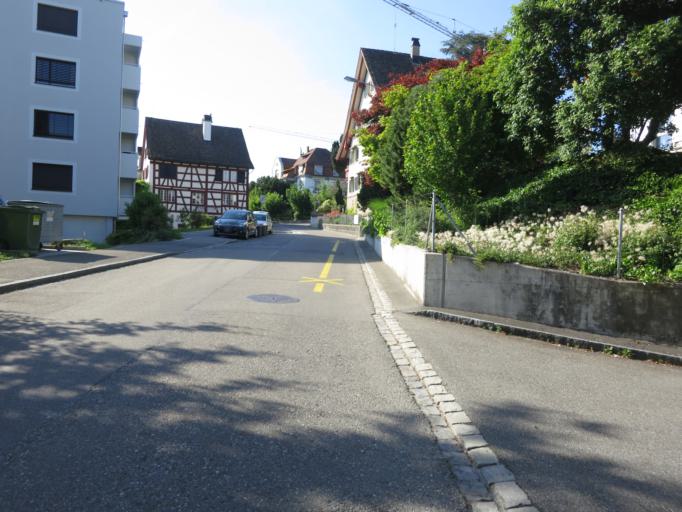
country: CH
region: Zurich
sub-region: Bezirk Meilen
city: Mannedorf
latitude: 47.2522
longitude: 8.6976
